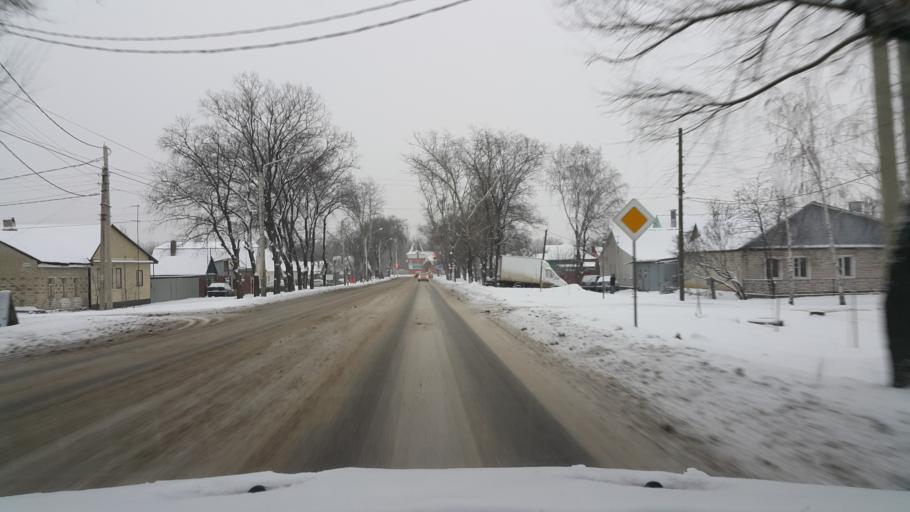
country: RU
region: Tambov
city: Pokrovo-Prigorodnoye
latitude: 52.7015
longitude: 41.4311
